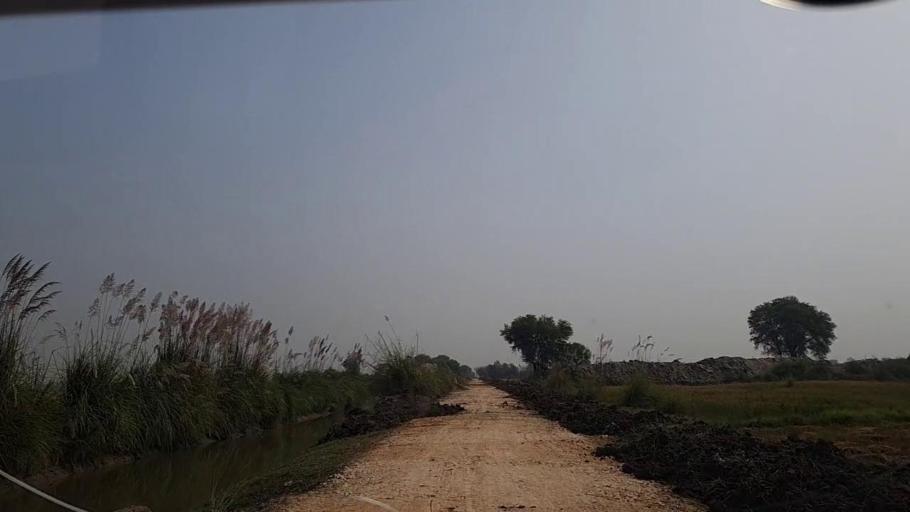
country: PK
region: Sindh
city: Shikarpur
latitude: 27.9205
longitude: 68.5791
